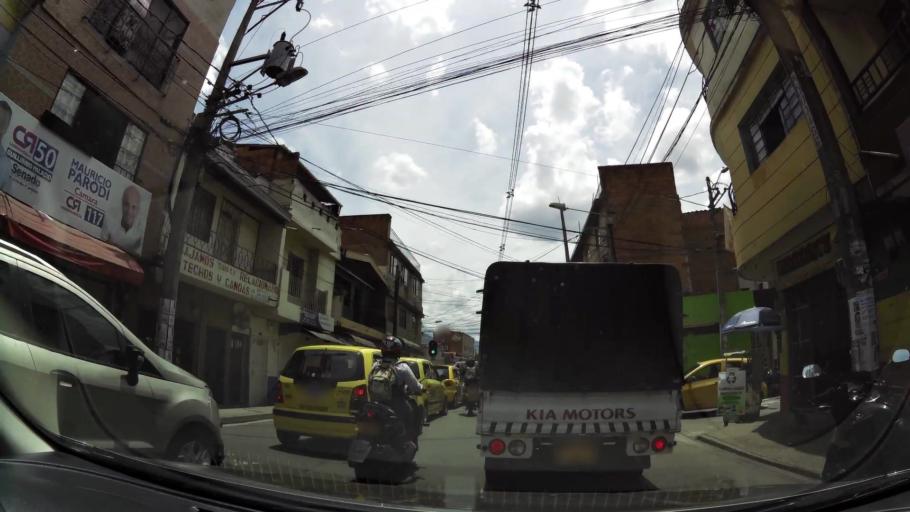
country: CO
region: Antioquia
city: Bello
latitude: 6.3343
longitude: -75.5601
